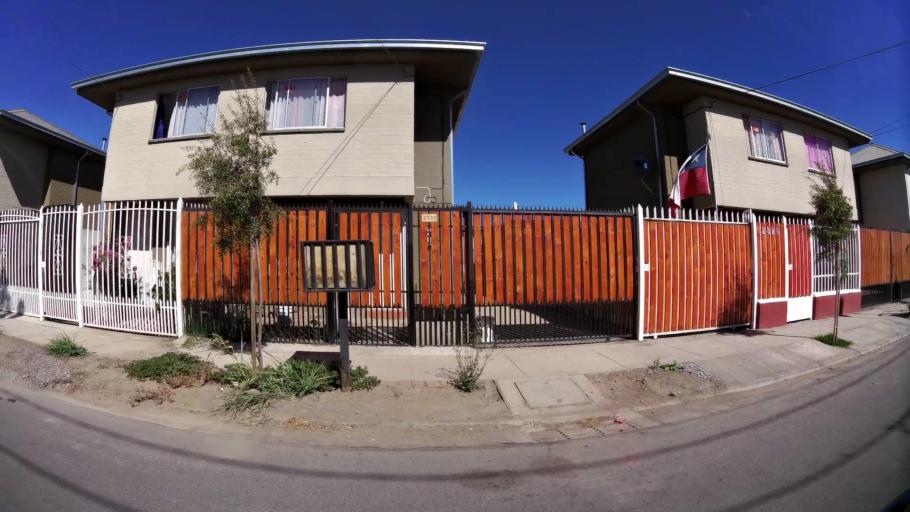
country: CL
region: O'Higgins
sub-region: Provincia de Cachapoal
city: Rancagua
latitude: -34.1779
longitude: -70.7705
